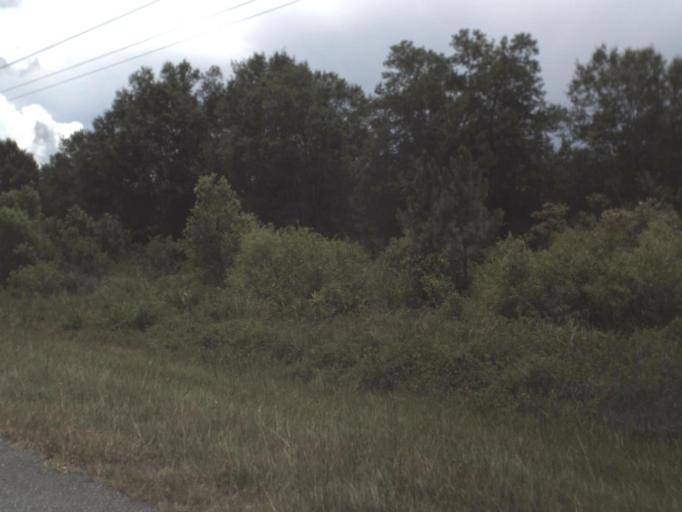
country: US
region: Florida
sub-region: Taylor County
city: Perry
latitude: 30.1429
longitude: -83.8462
